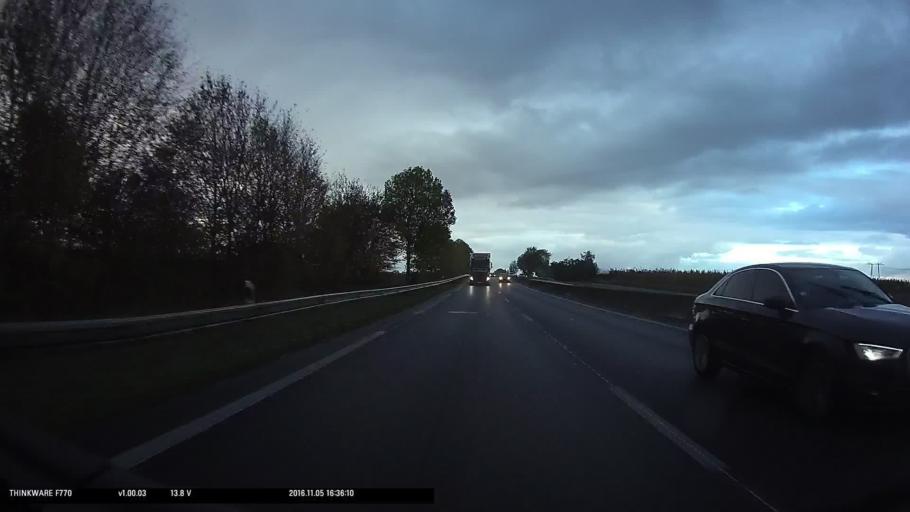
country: FR
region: Ile-de-France
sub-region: Departement du Val-d'Oise
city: Courdimanche
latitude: 49.0602
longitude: 1.9962
